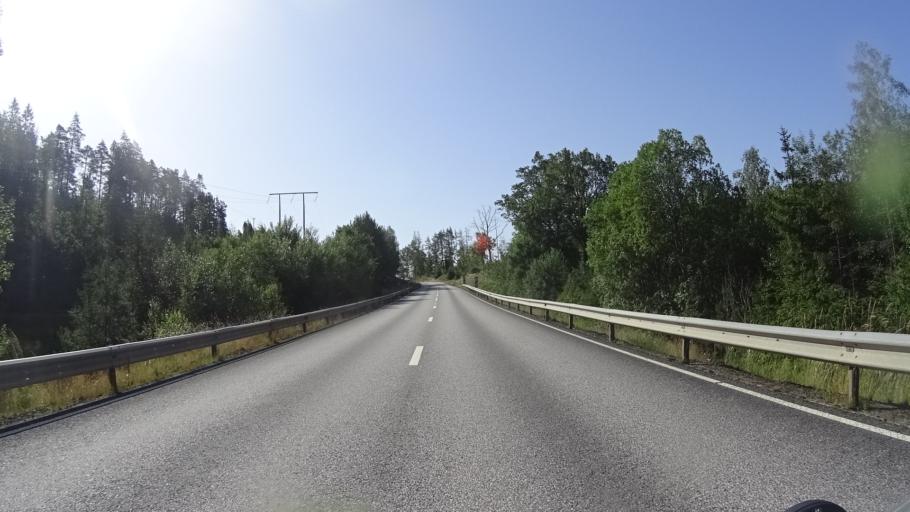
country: SE
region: Kalmar
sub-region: Vasterviks Kommun
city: Overum
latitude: 58.0479
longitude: 16.2103
